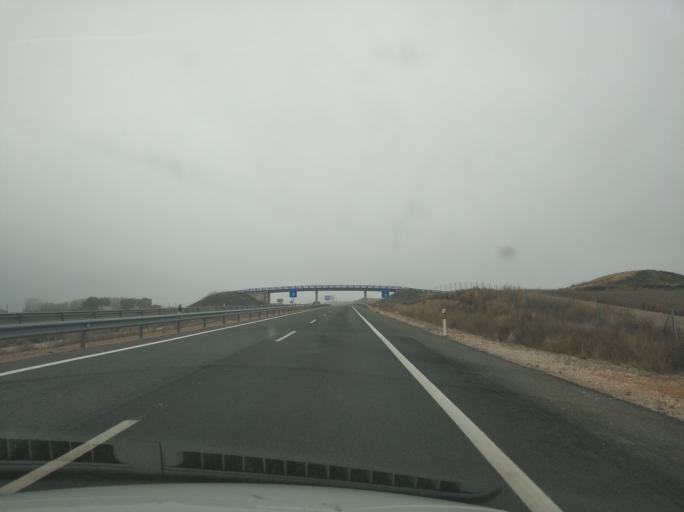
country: ES
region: Castille and Leon
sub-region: Provincia de Soria
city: Adradas
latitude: 41.3578
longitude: -2.4751
